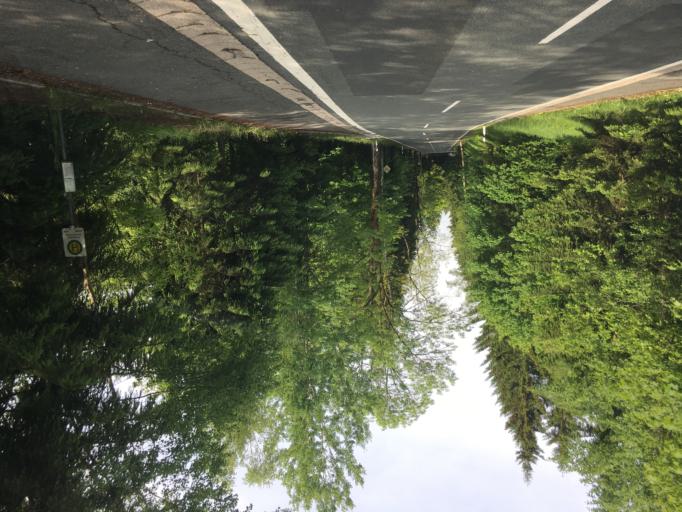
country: DE
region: Saxony
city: Frauenstein
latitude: 50.7813
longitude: 13.5505
